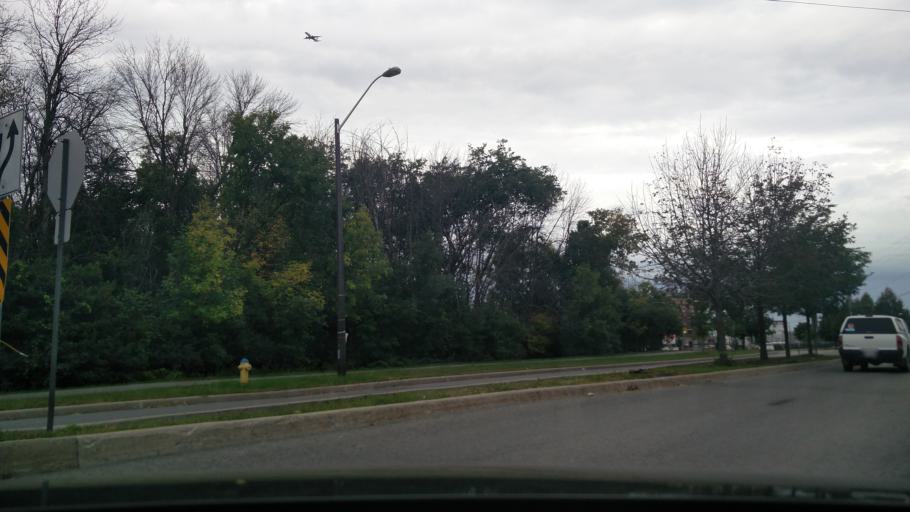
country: CA
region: Ontario
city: Bells Corners
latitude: 45.2854
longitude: -75.7421
